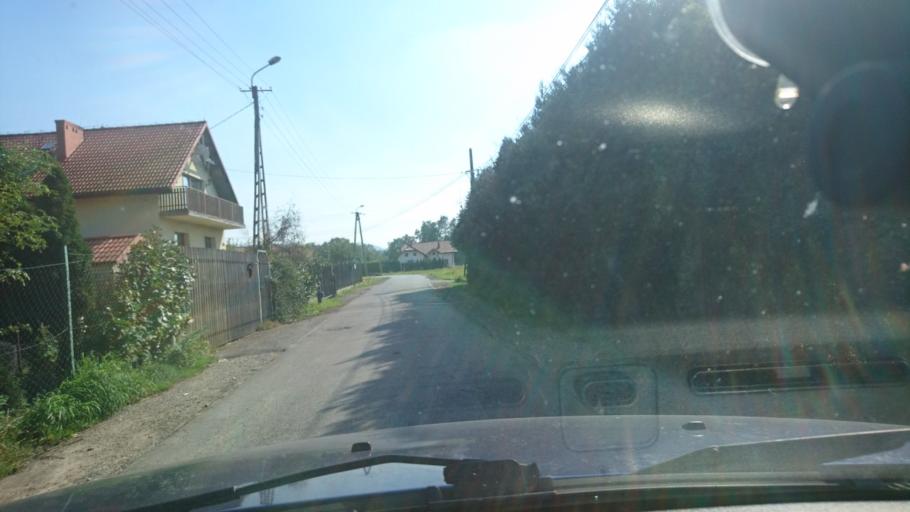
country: PL
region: Silesian Voivodeship
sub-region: Bielsko-Biala
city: Bielsko-Biala
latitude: 49.8531
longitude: 19.0678
